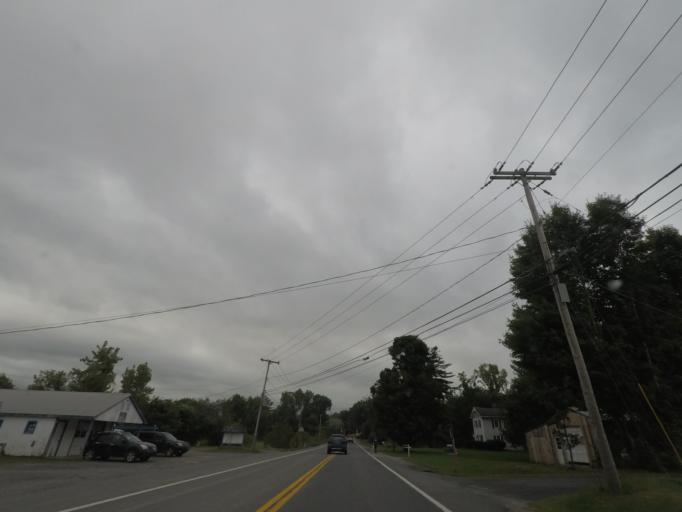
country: US
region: New York
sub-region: Rensselaer County
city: Hoosick Falls
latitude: 42.8791
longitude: -73.3574
